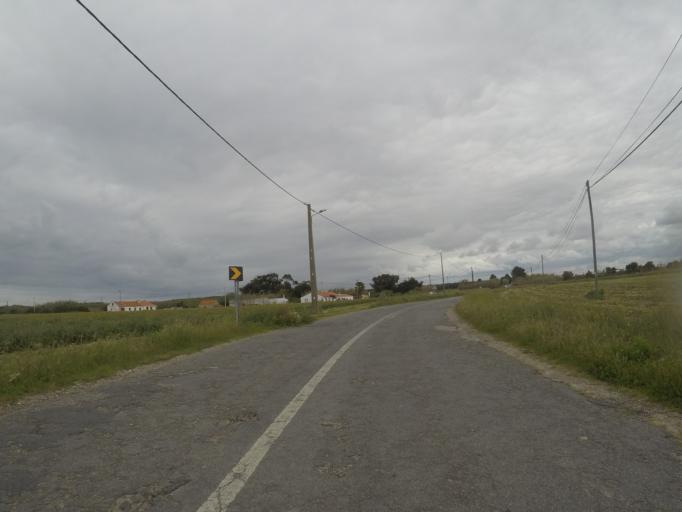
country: PT
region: Beja
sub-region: Odemira
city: Vila Nova de Milfontes
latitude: 37.5994
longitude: -8.8055
